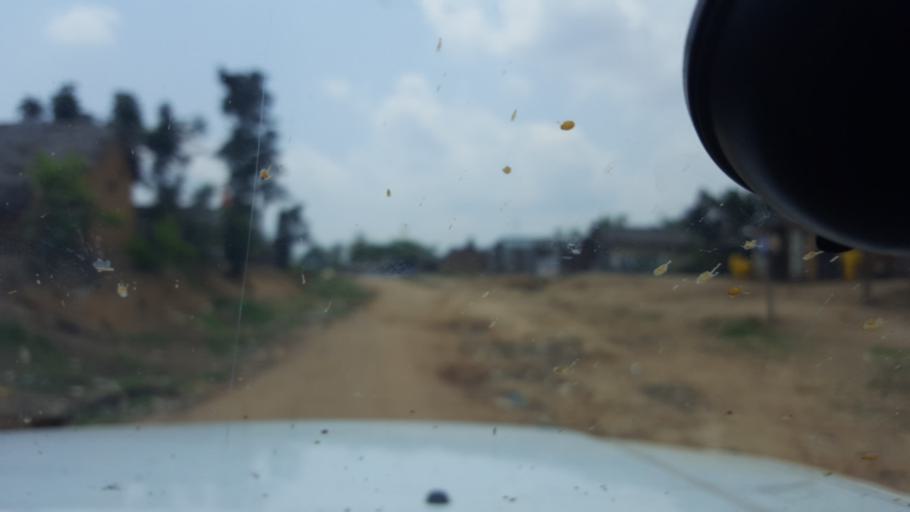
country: CD
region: Bandundu
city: Mushie
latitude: -3.7437
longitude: 16.6518
